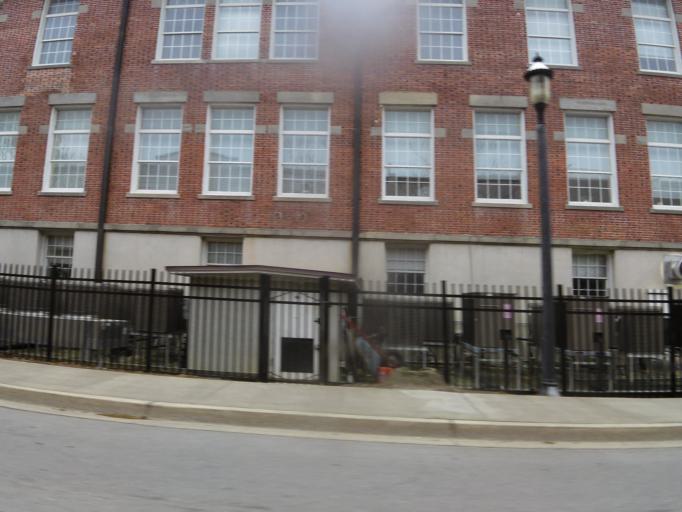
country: US
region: Florida
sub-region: Saint Johns County
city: Saint Augustine
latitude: 29.8980
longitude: -81.3158
